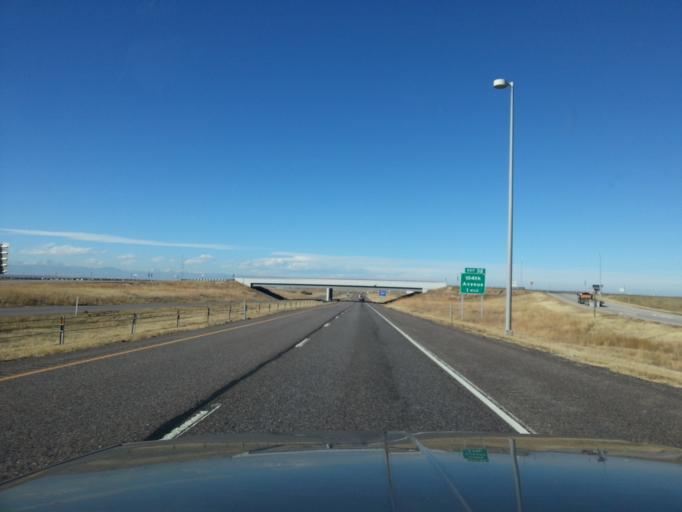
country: US
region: Colorado
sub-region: Adams County
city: Brighton
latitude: 39.8687
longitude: -104.7540
